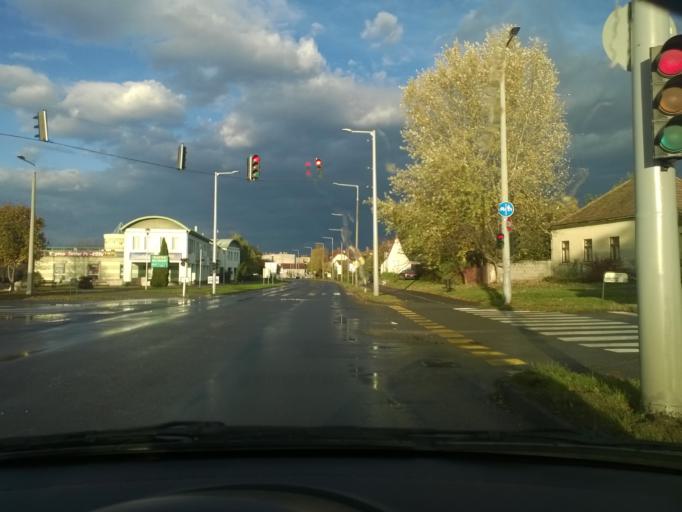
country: HU
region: Bacs-Kiskun
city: Kalocsa
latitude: 46.5236
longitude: 18.9838
